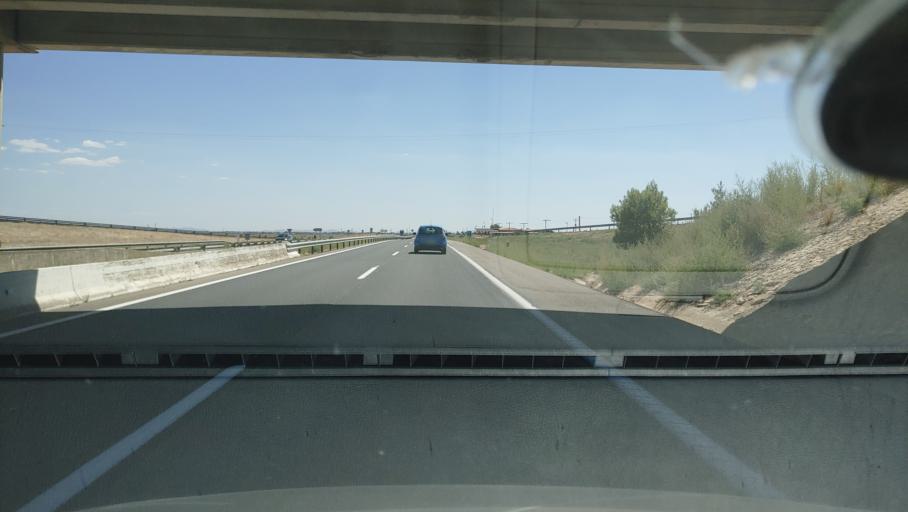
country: ES
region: Castille-La Mancha
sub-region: Provincia de Ciudad Real
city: Villarta de San Juan
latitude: 39.1674
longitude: -3.3933
